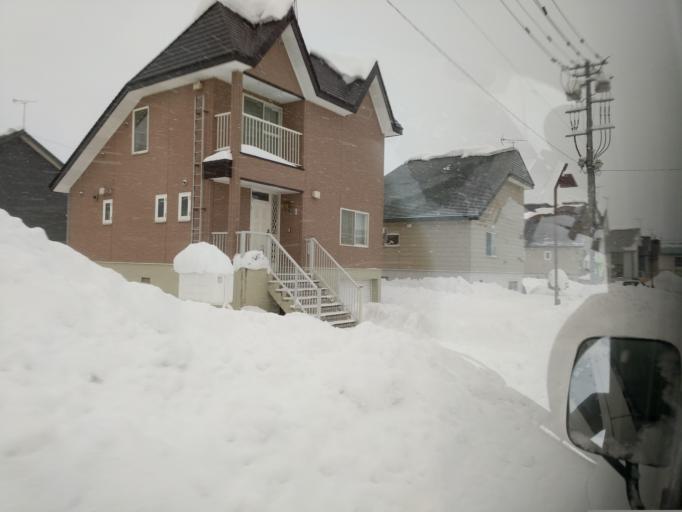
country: JP
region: Hokkaido
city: Niseko Town
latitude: 42.8980
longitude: 140.7473
